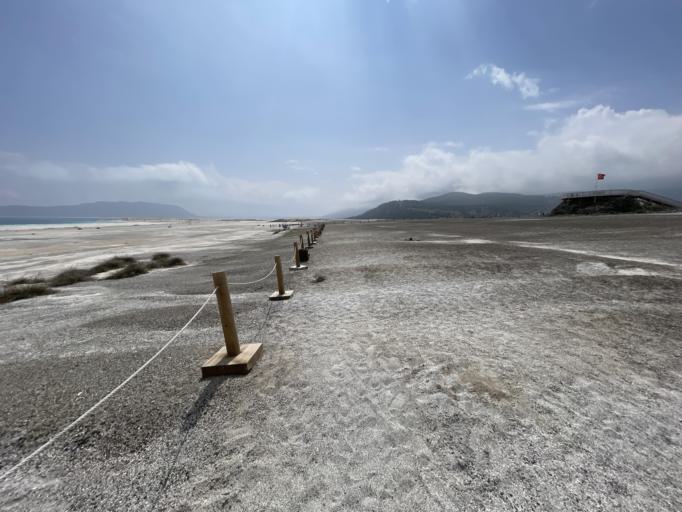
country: TR
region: Burdur
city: Yesilova
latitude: 37.5348
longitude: 29.6456
